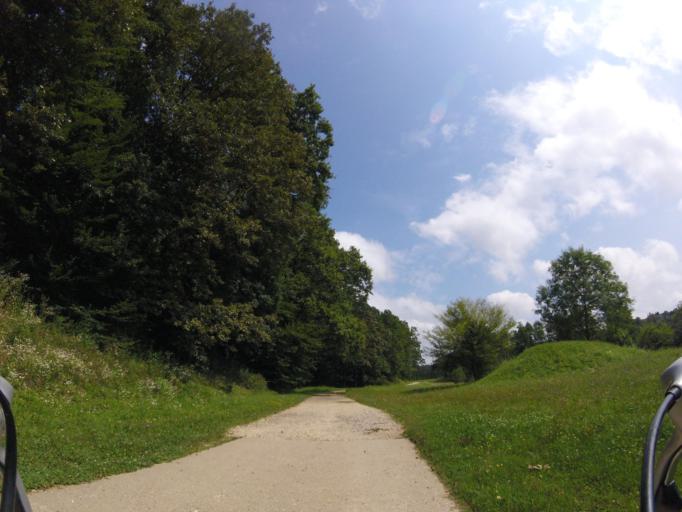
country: HU
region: Zala
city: Nagykanizsa
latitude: 46.4432
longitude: 17.0433
